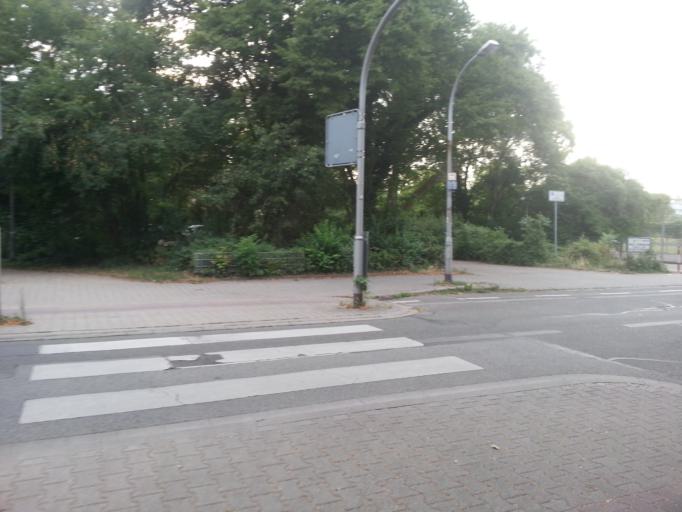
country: DE
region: Rheinland-Pfalz
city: Ludwigshafen am Rhein
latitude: 49.4609
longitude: 8.4720
